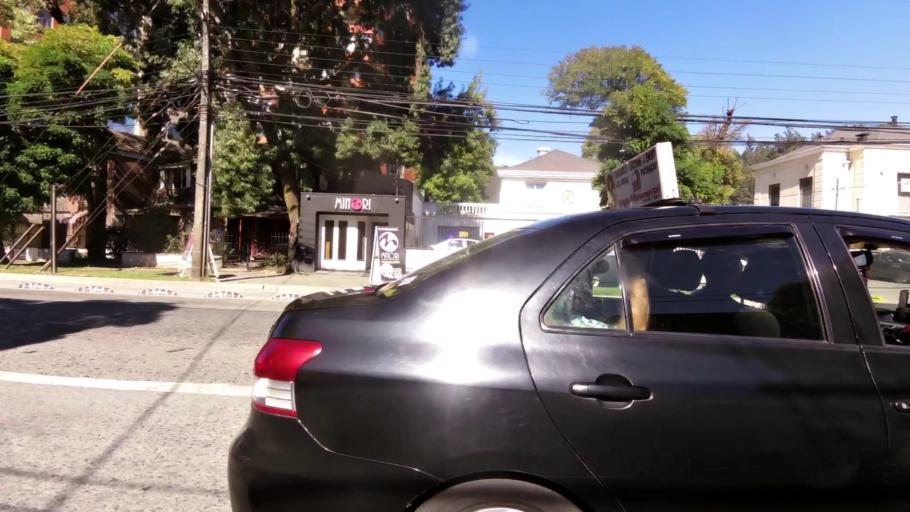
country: CL
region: Biobio
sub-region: Provincia de Concepcion
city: Concepcion
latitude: -36.8211
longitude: -73.0359
